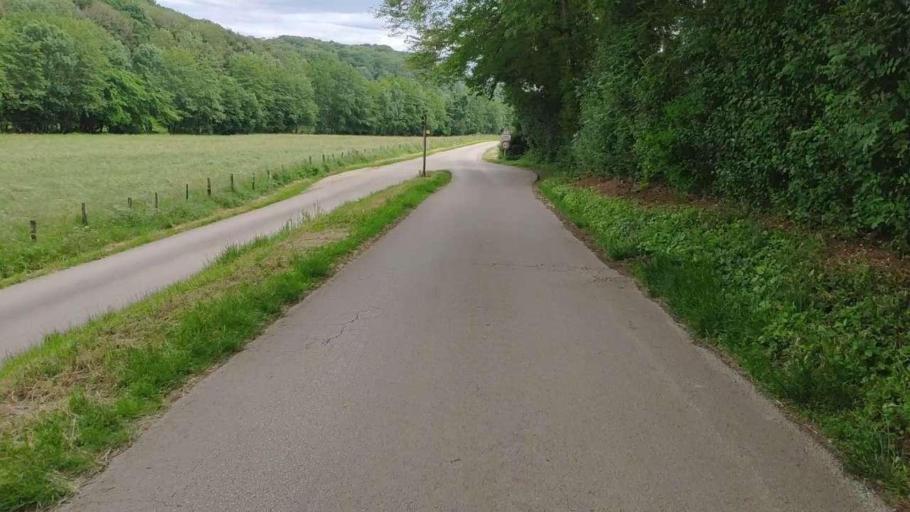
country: FR
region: Franche-Comte
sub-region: Departement du Jura
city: Montmorot
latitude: 46.7420
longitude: 5.5317
